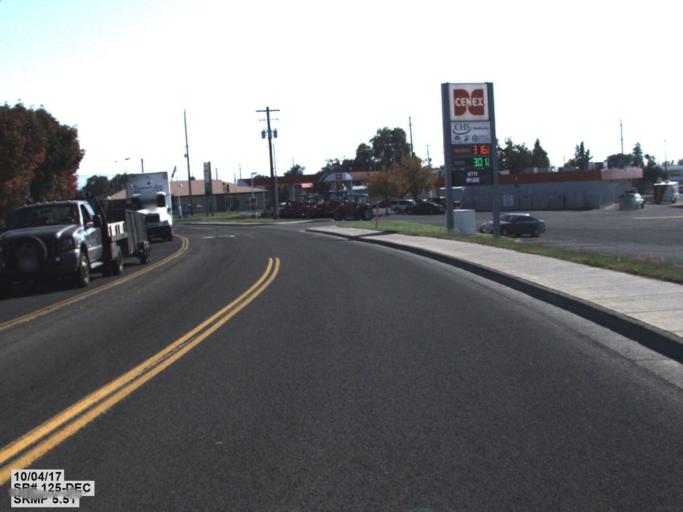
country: US
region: Washington
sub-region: Walla Walla County
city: Walla Walla
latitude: 46.0653
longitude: -118.3499
